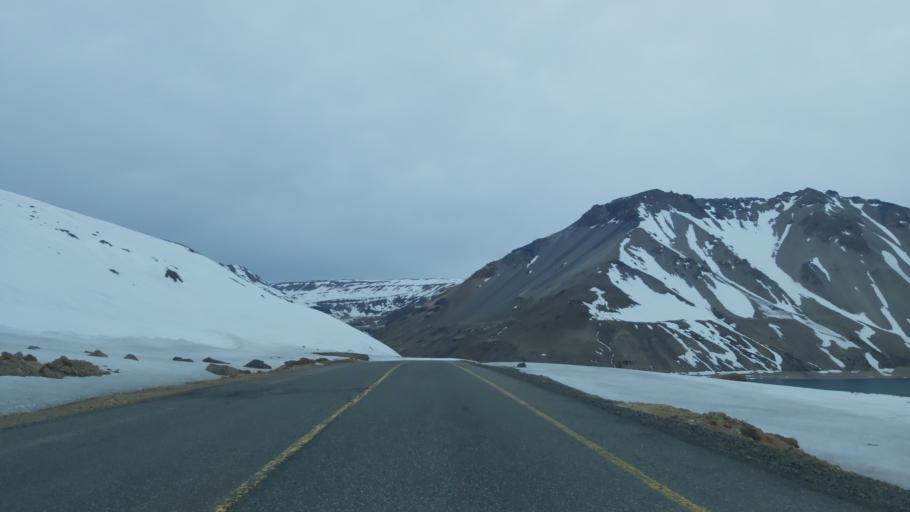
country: CL
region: Maule
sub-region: Provincia de Linares
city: Colbun
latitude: -36.0070
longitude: -70.4776
